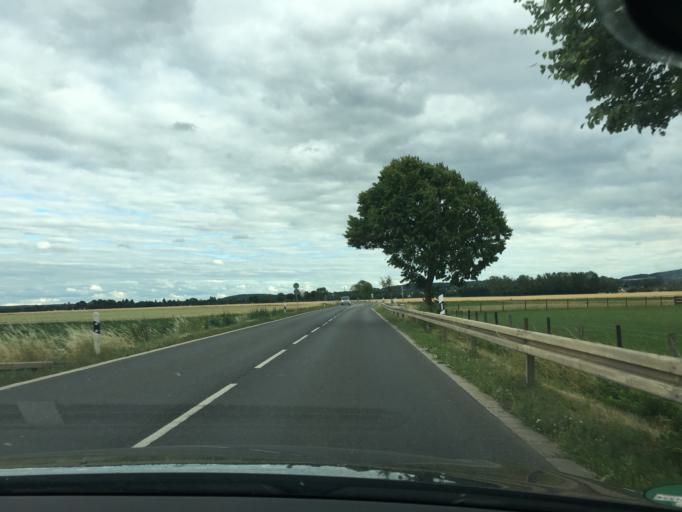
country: DE
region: North Rhine-Westphalia
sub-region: Regierungsbezirk Koln
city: Dueren
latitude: 50.7866
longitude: 6.4443
